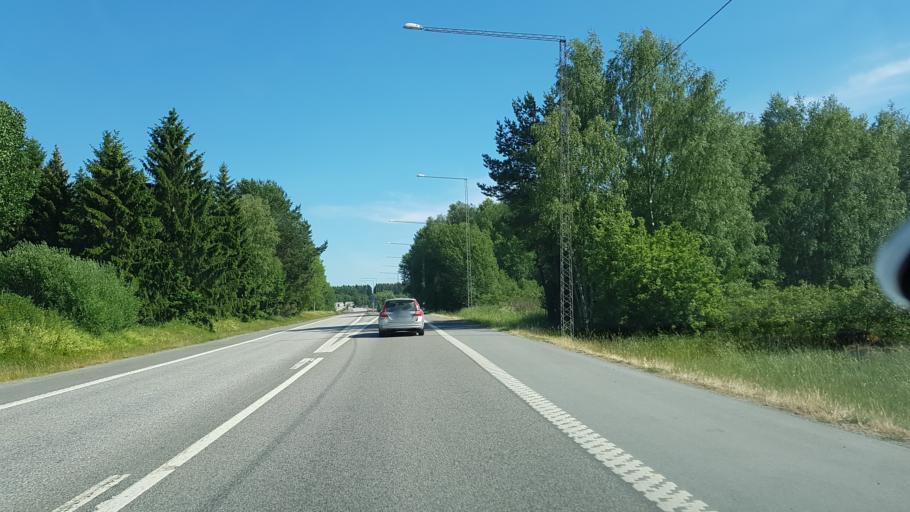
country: SE
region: Stockholm
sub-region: Sigtuna Kommun
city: Rosersberg
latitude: 59.6084
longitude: 17.8908
